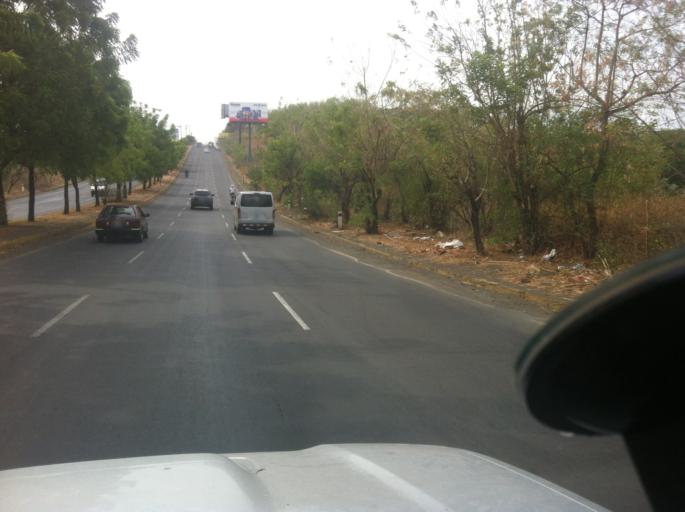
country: NI
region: Managua
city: Ciudad Sandino
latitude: 12.1152
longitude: -86.3097
